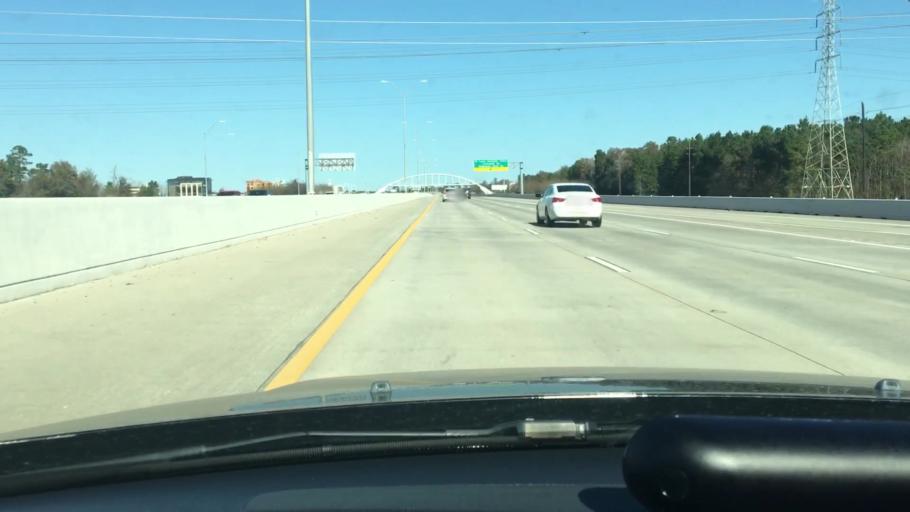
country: US
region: Texas
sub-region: Harris County
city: Sheldon
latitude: 29.9113
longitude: -95.2016
